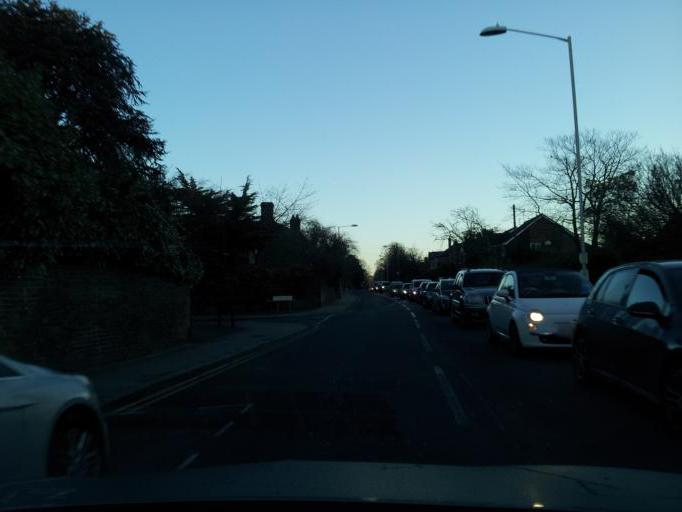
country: GB
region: England
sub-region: Essex
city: Chelmsford
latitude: 51.7382
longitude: 0.4864
